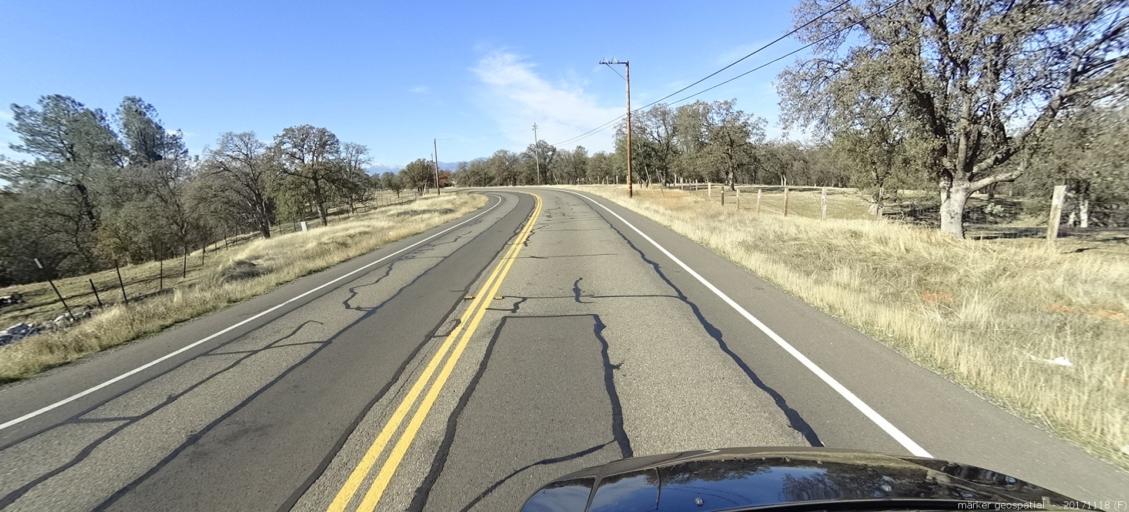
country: US
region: California
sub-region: Shasta County
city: Anderson
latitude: 40.4408
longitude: -122.3419
